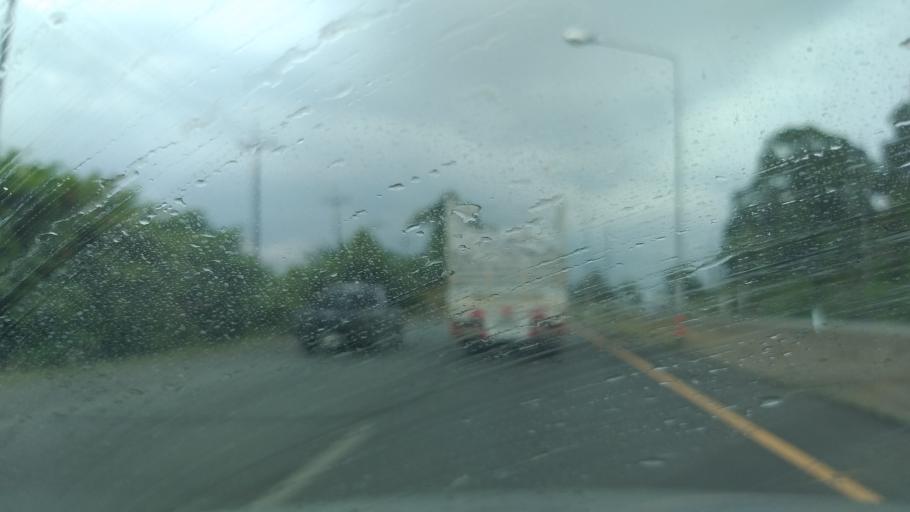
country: TH
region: Chanthaburi
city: Khlung
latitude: 12.4306
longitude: 102.3123
